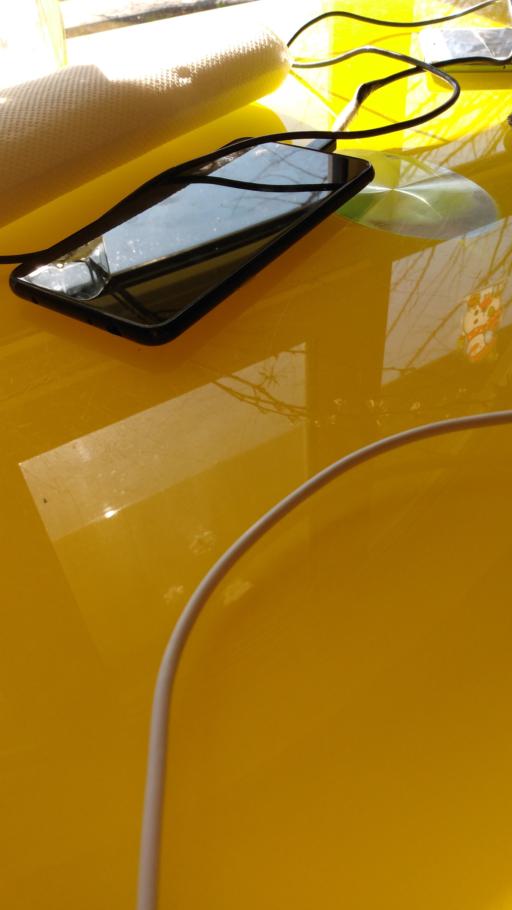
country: RU
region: Novgorod
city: Kresttsy
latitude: 58.4793
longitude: 32.2714
